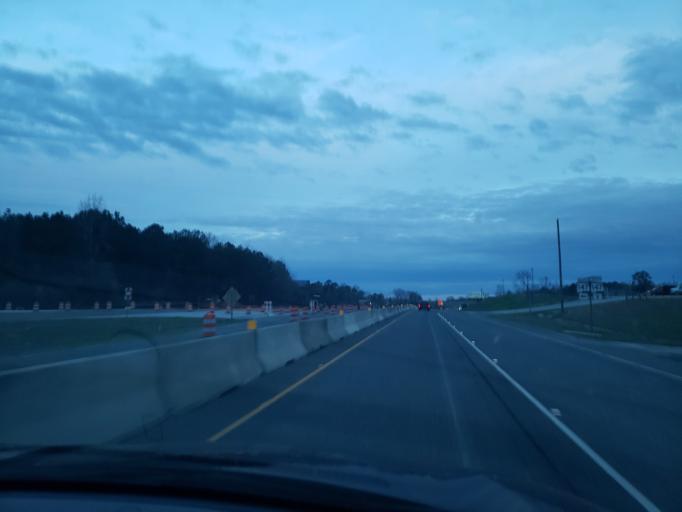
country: US
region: Alabama
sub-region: Lee County
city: Auburn
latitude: 32.6762
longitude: -85.4857
